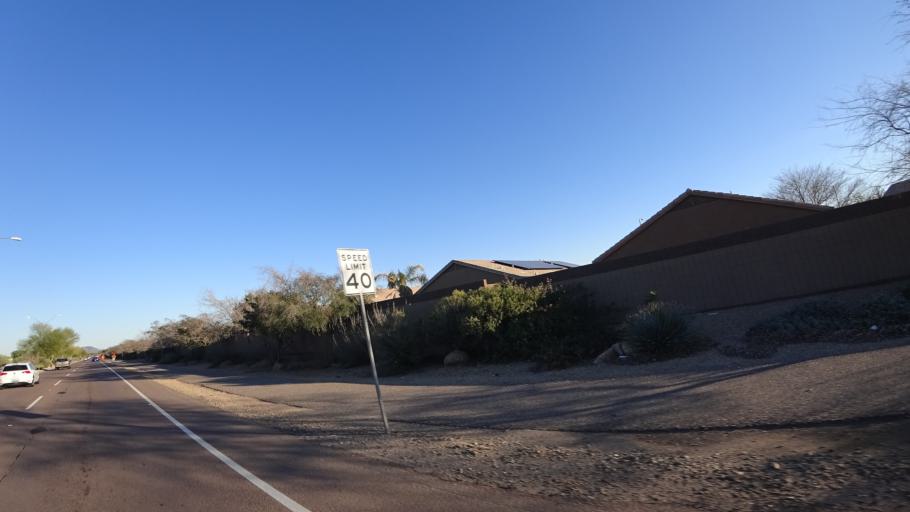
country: US
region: Arizona
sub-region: Maricopa County
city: Sun City
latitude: 33.6744
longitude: -112.2632
